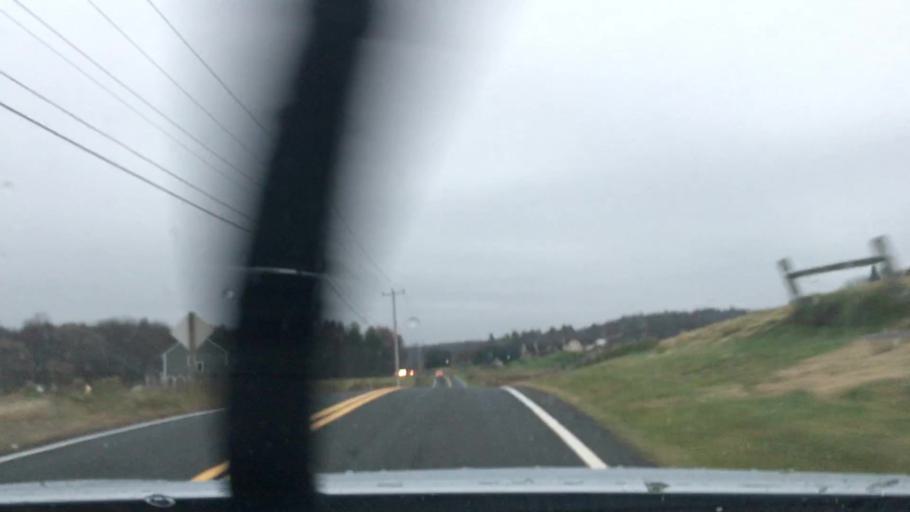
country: US
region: Massachusetts
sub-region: Hampden County
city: Southwick
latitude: 42.0909
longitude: -72.7765
